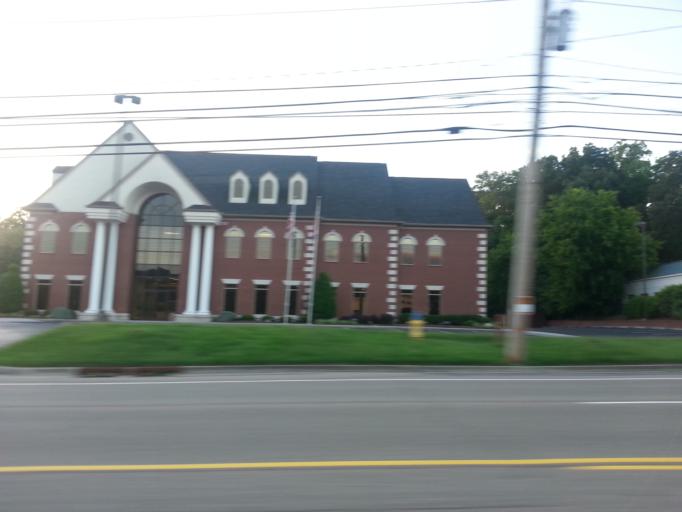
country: US
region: Tennessee
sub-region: Knox County
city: Farragut
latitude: 35.8990
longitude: -84.1281
